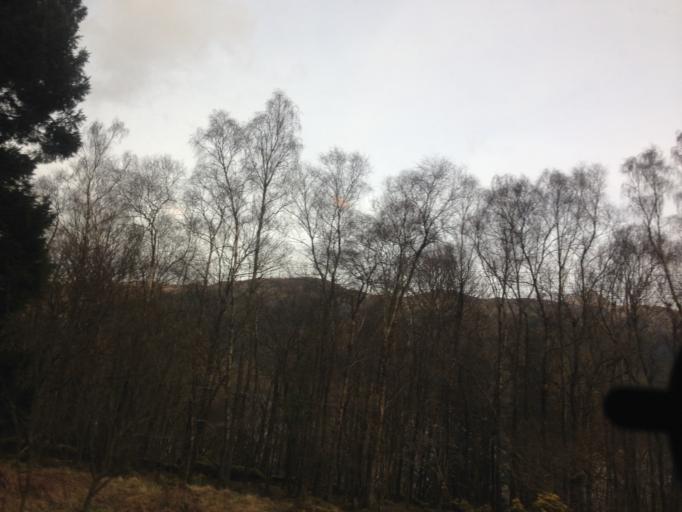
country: GB
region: Scotland
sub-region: Argyll and Bute
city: Garelochhead
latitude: 56.2097
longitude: -4.7046
